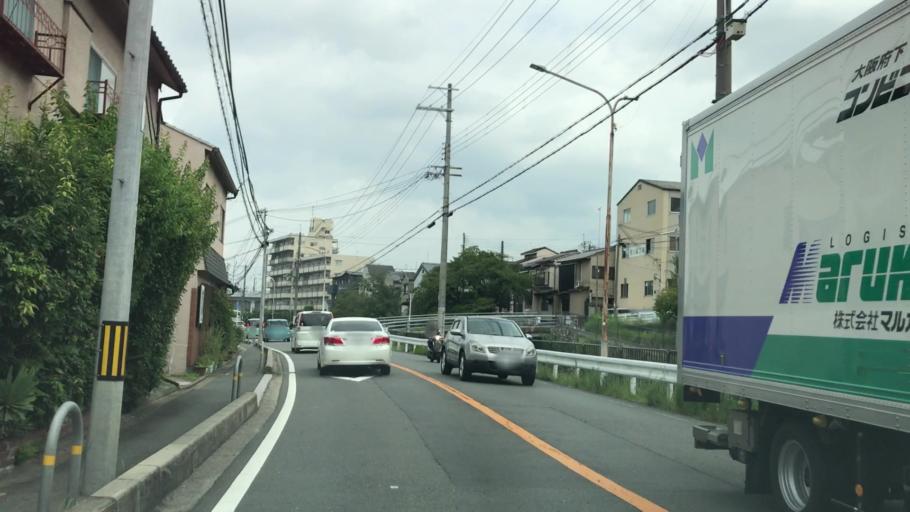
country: JP
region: Kyoto
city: Kyoto
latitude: 34.9785
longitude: 135.7692
